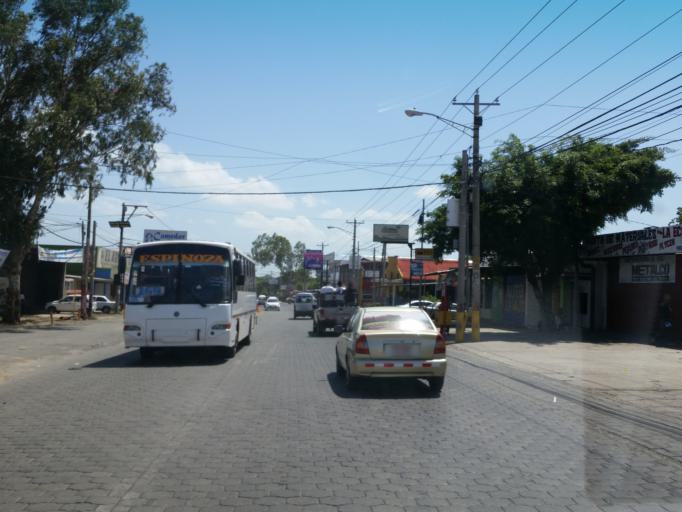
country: NI
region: Managua
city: Managua
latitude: 12.1350
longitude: -86.1984
